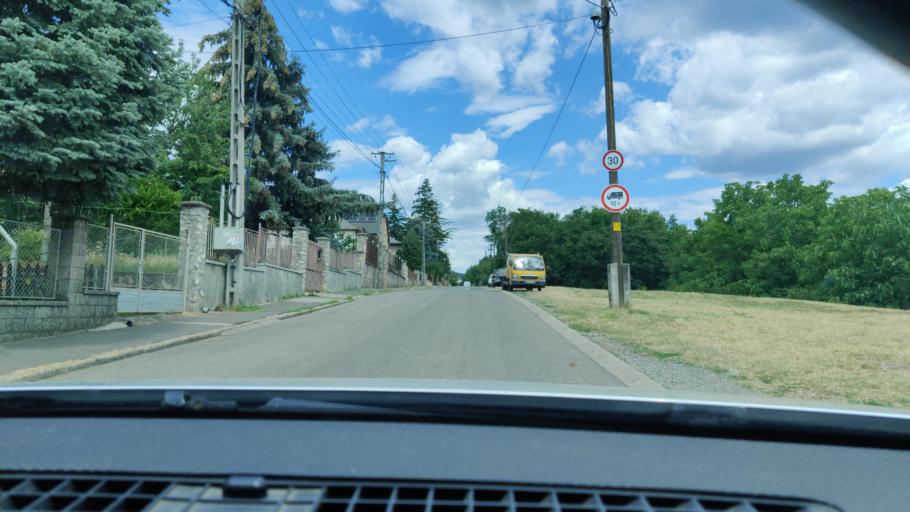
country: HU
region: Baranya
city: Pecs
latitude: 46.0870
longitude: 18.2620
